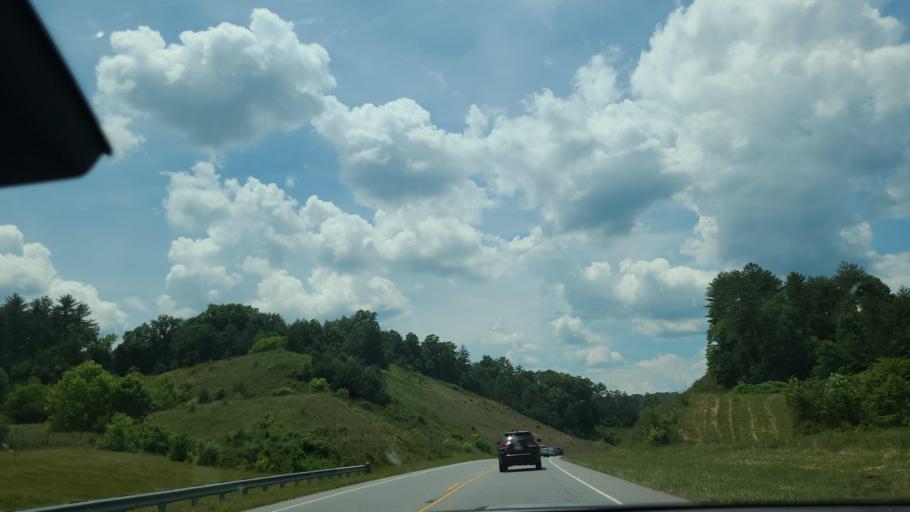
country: US
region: North Carolina
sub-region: Cherokee County
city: Murphy
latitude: 35.0701
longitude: -84.0093
